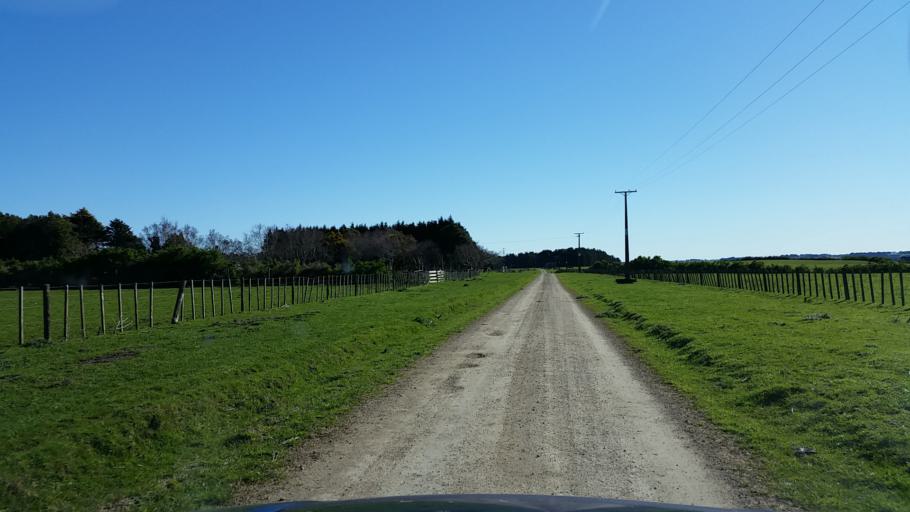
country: NZ
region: Taranaki
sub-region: South Taranaki District
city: Patea
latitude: -39.7897
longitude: 174.7631
